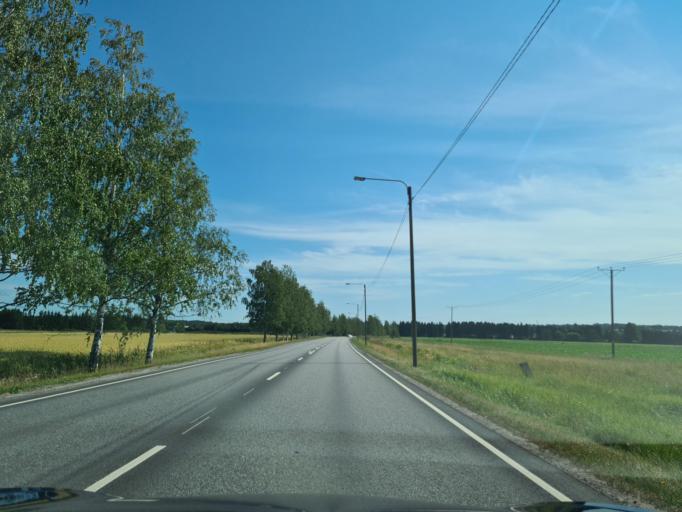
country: FI
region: Varsinais-Suomi
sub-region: Turku
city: Paimio
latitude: 60.4541
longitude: 22.6604
